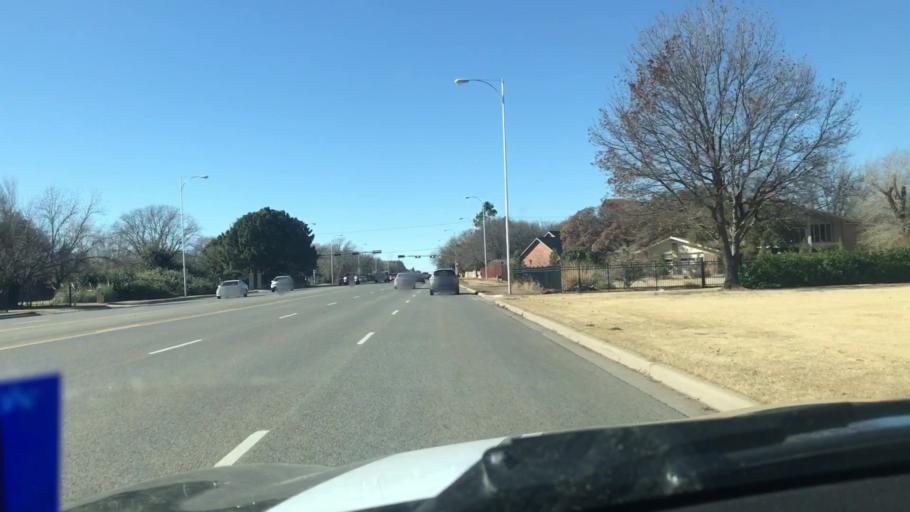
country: US
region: Texas
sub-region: Lubbock County
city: Lubbock
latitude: 33.5779
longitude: -101.9204
